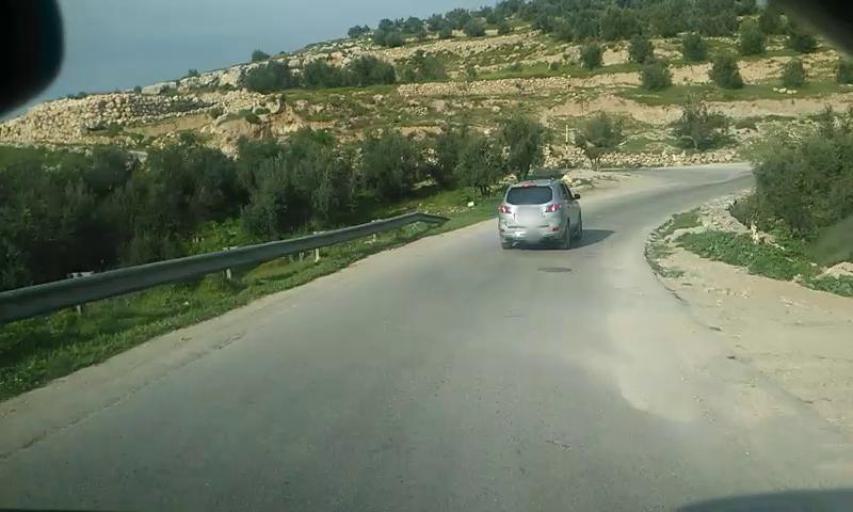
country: PS
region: West Bank
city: Nuba
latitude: 31.6145
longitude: 35.0194
